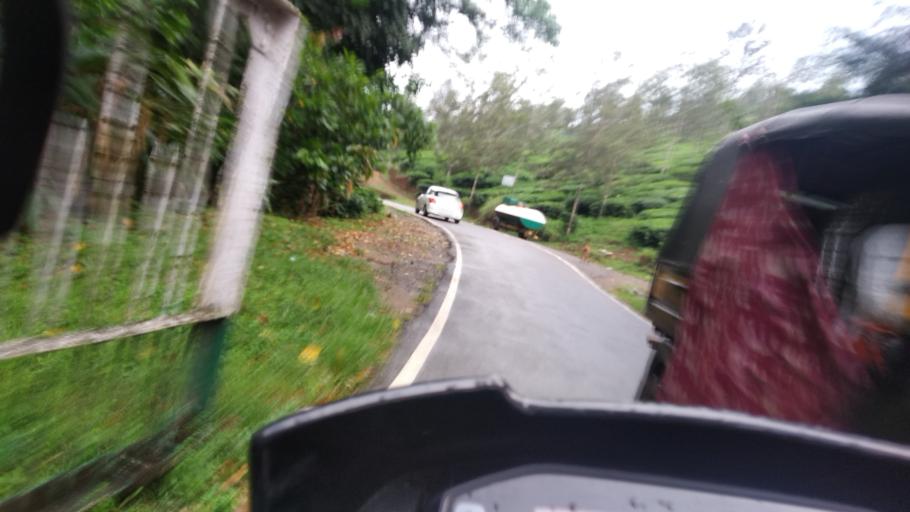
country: IN
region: Tamil Nadu
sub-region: Theni
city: Gudalur
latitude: 9.5696
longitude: 77.0804
